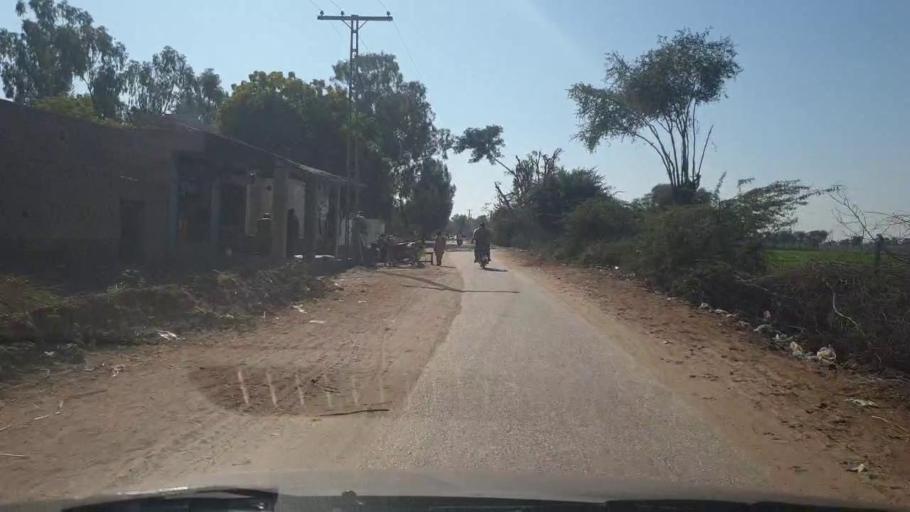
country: PK
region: Sindh
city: Bozdar
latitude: 27.0938
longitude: 68.6250
